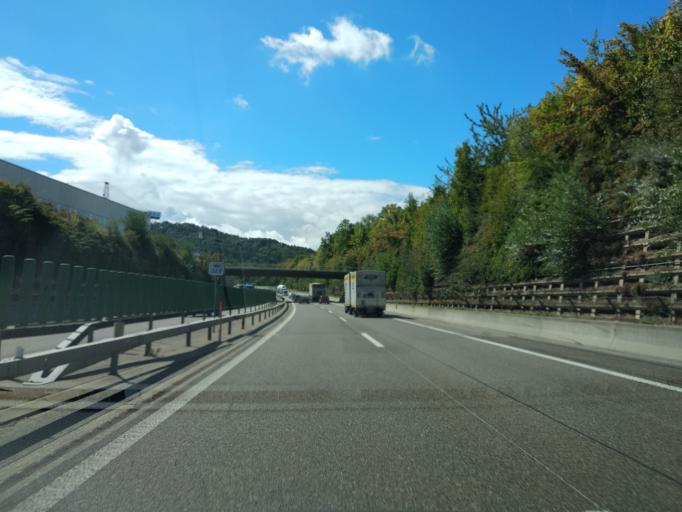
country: CH
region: Zurich
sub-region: Bezirk Winterthur
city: Wuelflingen (Kreis 6) / Haerti
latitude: 47.5119
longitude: 8.6884
